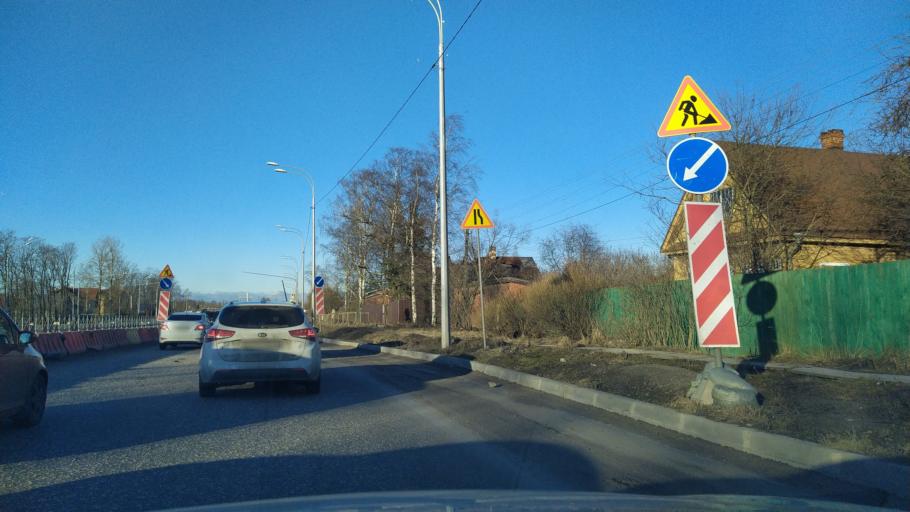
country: RU
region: St.-Petersburg
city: Gorelovo
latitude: 59.7592
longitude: 30.1109
